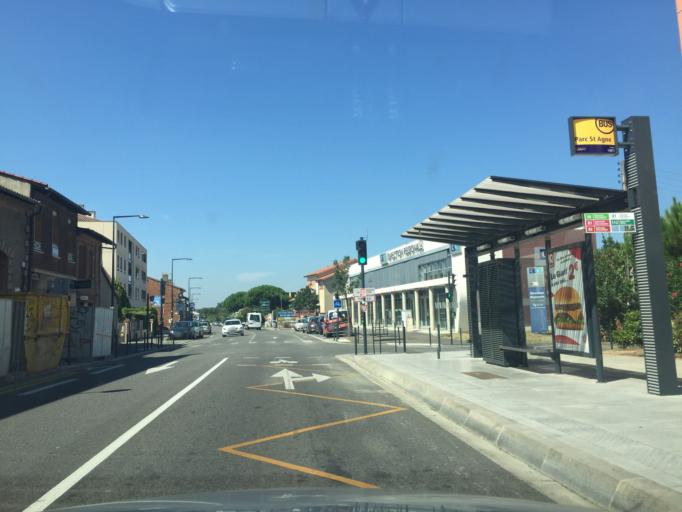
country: FR
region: Midi-Pyrenees
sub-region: Departement de la Haute-Garonne
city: Ramonville-Saint-Agne
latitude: 43.5528
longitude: 1.4689
